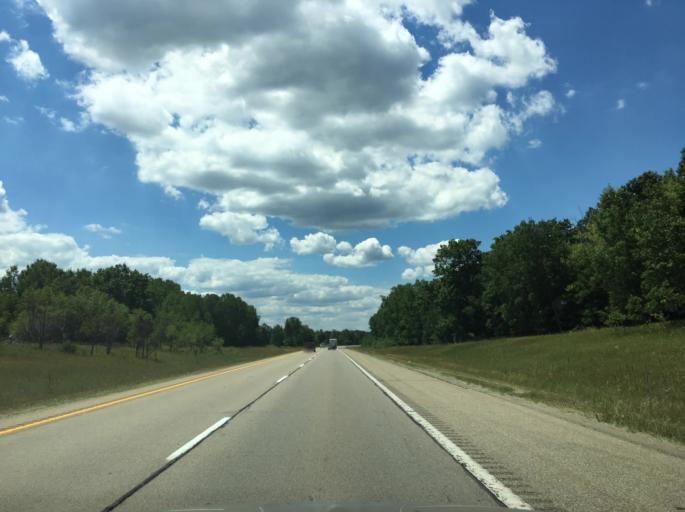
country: US
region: Michigan
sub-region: Clare County
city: Clare
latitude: 43.8791
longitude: -84.8165
